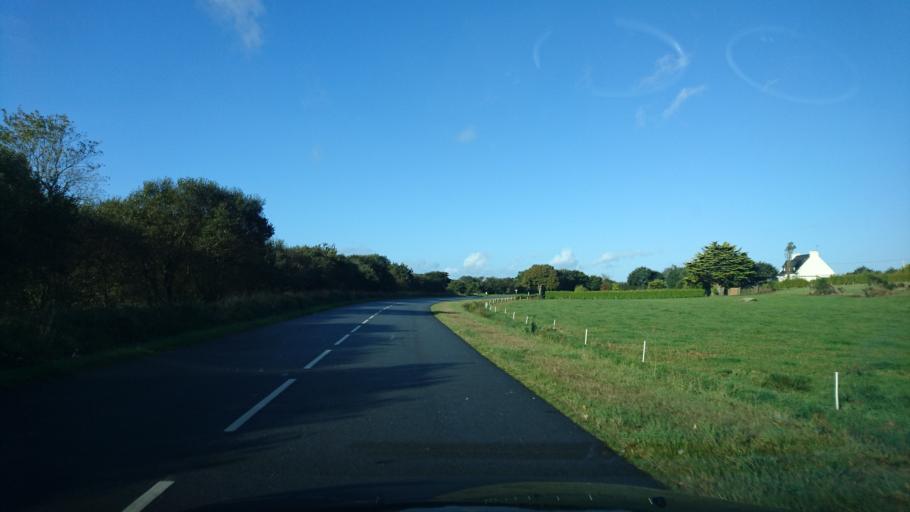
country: FR
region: Brittany
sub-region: Departement du Finistere
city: Plouarzel
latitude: 48.4383
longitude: -4.7292
